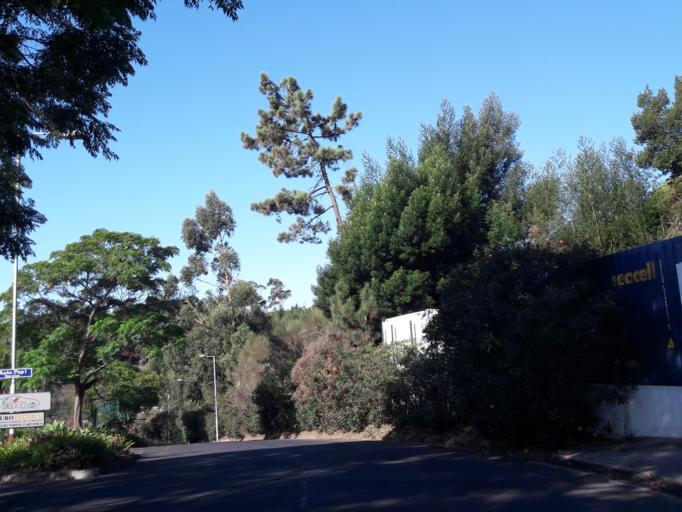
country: PT
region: Madeira
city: Canico
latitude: 32.6524
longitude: -16.8619
